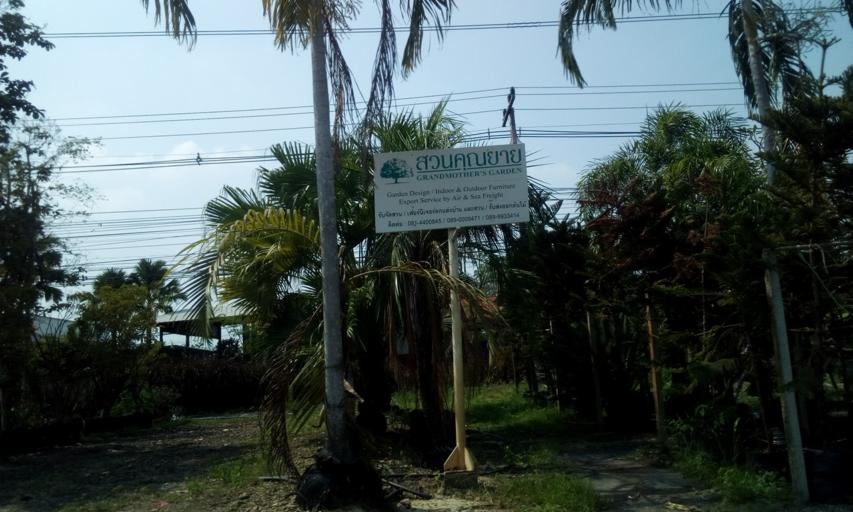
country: TH
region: Nakhon Nayok
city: Ongkharak
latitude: 14.0966
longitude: 100.9439
